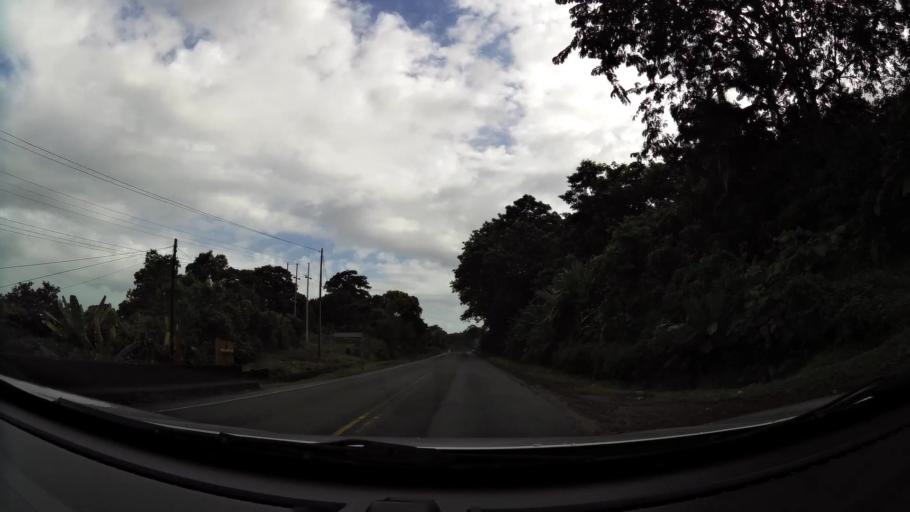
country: CR
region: Limon
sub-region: Canton de Siquirres
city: Pacuarito
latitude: 10.0935
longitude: -83.4854
